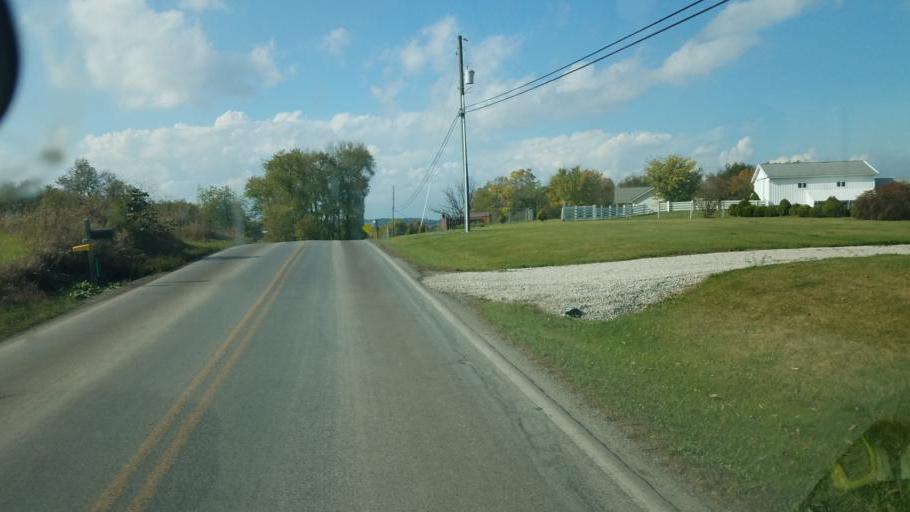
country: US
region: Ohio
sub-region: Wayne County
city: Apple Creek
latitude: 40.6700
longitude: -81.8652
